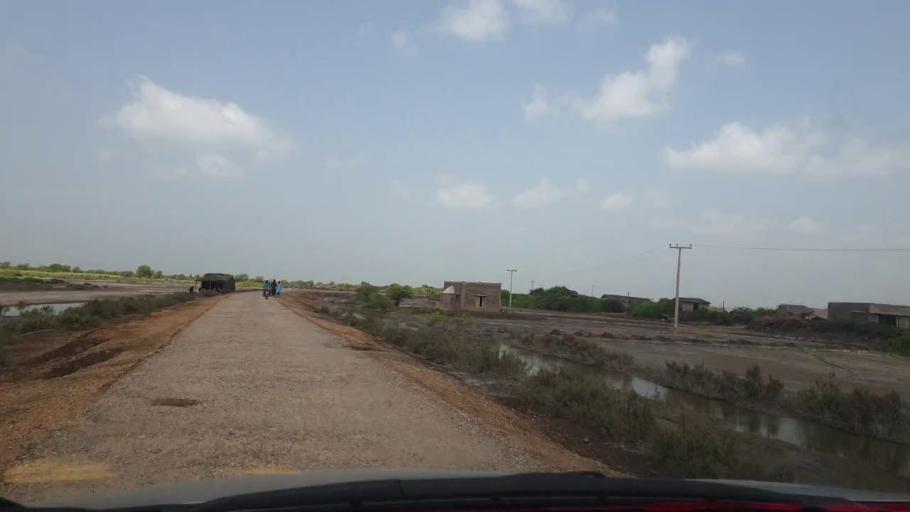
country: PK
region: Sindh
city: Rajo Khanani
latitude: 24.9222
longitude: 68.8981
